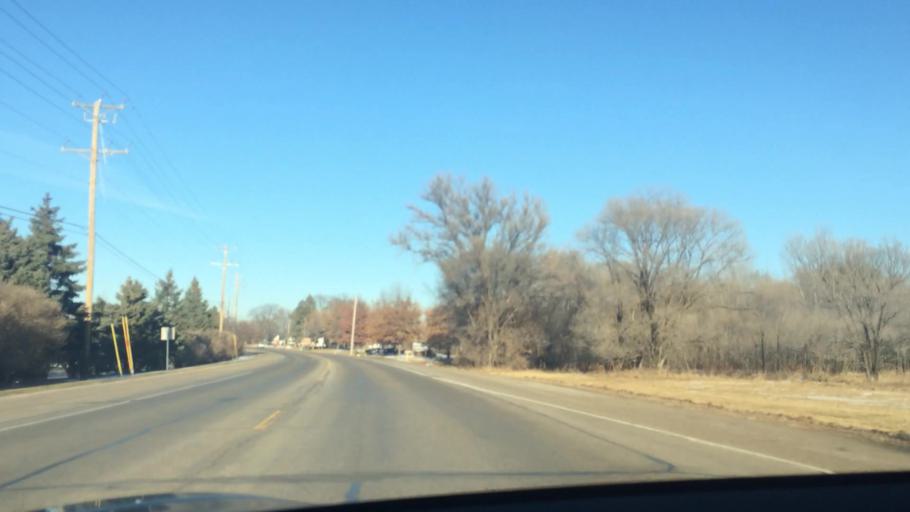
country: US
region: Minnesota
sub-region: Anoka County
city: Circle Pines
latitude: 45.1608
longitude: -93.1247
